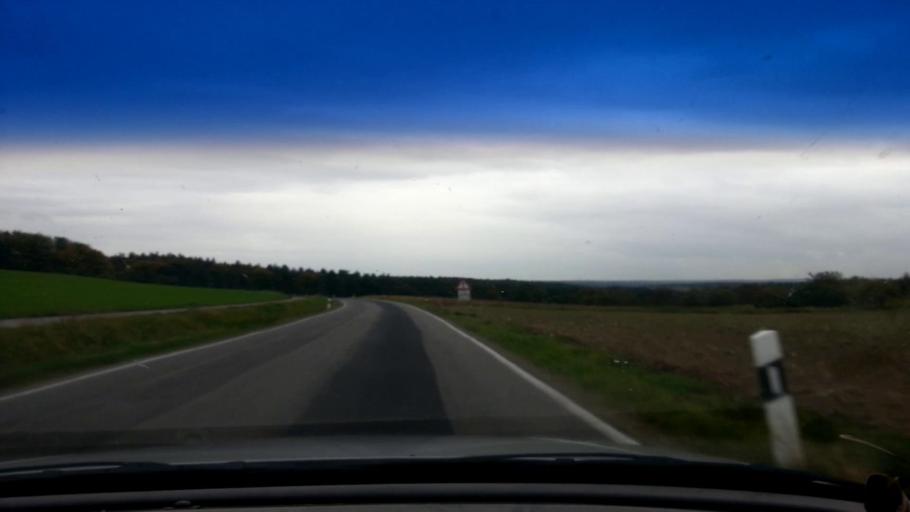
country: DE
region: Bavaria
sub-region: Upper Franconia
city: Priesendorf
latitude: 49.9009
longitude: 10.6580
